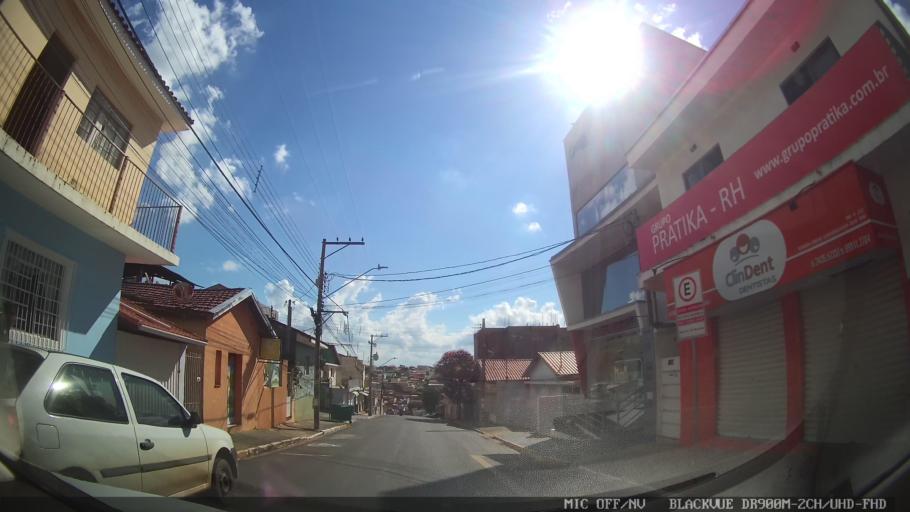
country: BR
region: Minas Gerais
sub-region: Extrema
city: Extrema
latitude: -22.8572
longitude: -46.3212
